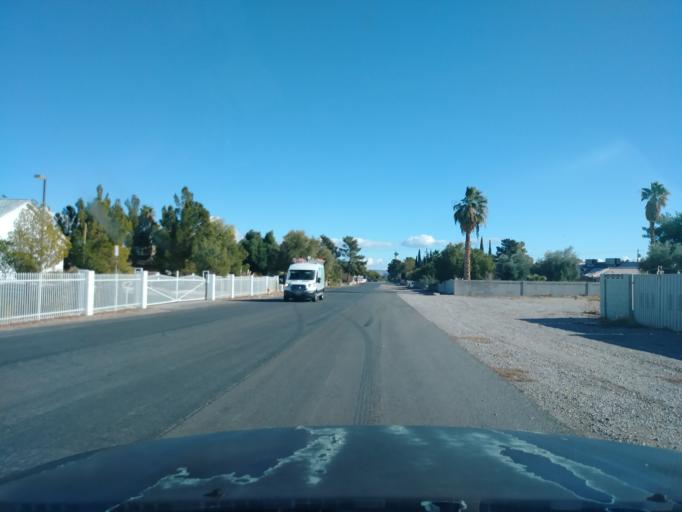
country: US
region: Nevada
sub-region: Clark County
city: Spring Valley
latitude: 36.1481
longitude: -115.2164
